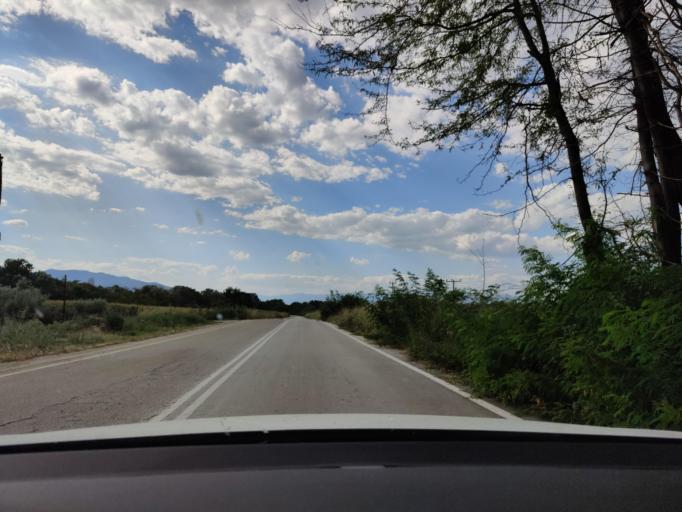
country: GR
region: Central Macedonia
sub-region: Nomos Serron
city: Strymoniko
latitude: 41.0526
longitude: 23.3212
